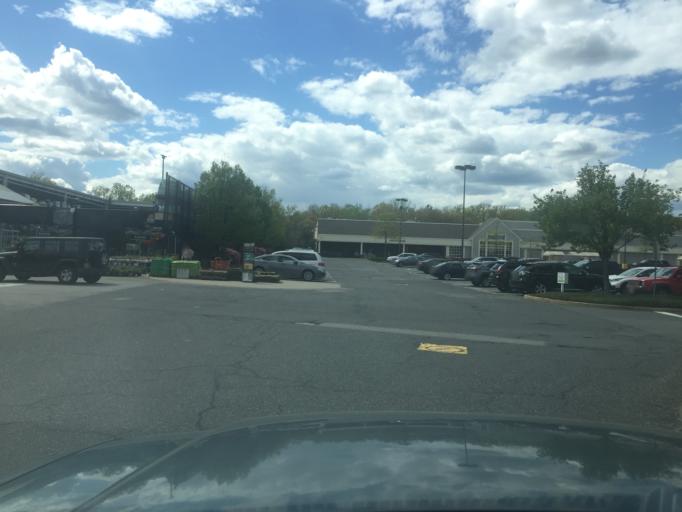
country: US
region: Massachusetts
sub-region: Norfolk County
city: Norwood
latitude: 42.1639
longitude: -71.2004
